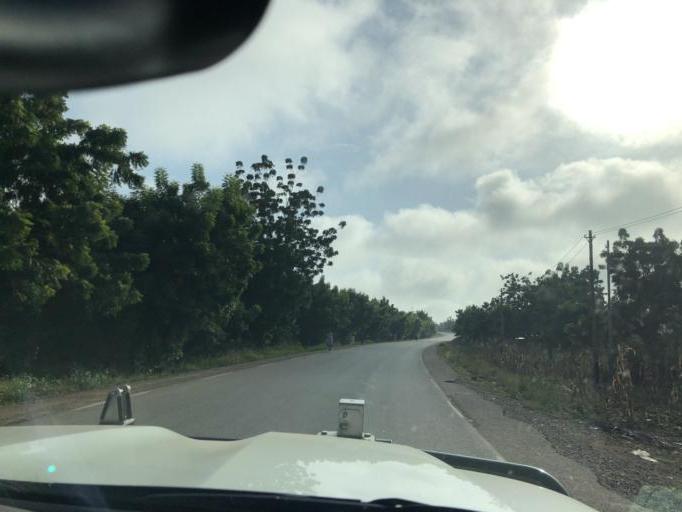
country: CM
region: North Province
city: Pitoa
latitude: 9.4938
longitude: 13.6844
